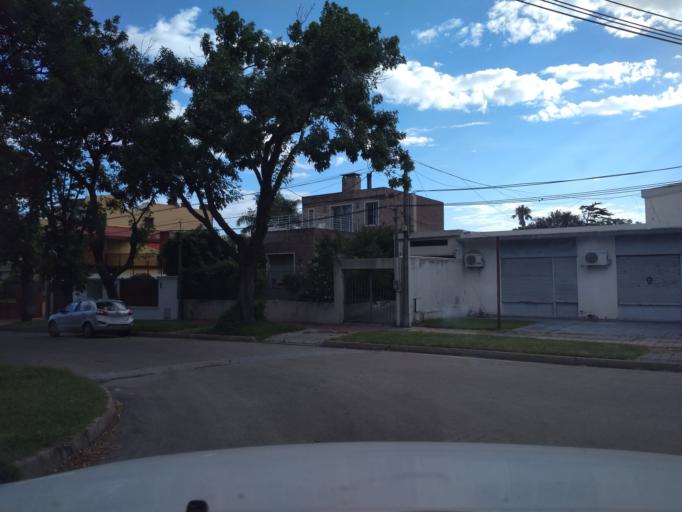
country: UY
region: Canelones
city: Paso de Carrasco
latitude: -34.8938
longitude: -56.0872
